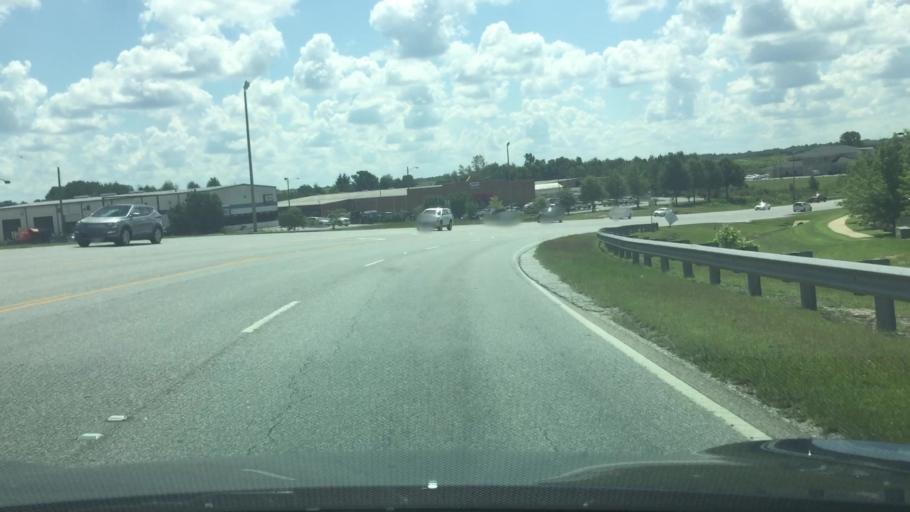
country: US
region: Alabama
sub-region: Lee County
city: Auburn
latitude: 32.6087
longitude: -85.4425
